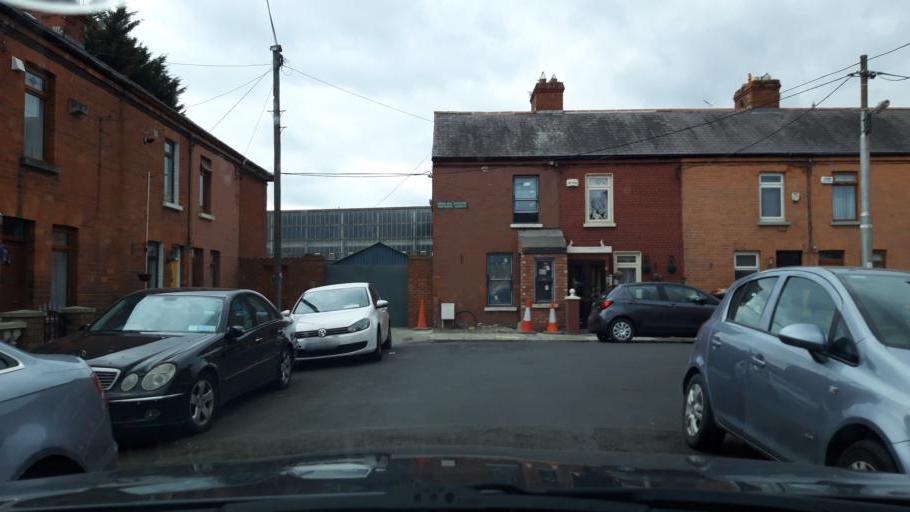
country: IE
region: Leinster
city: Crumlin
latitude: 53.3362
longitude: -6.3318
